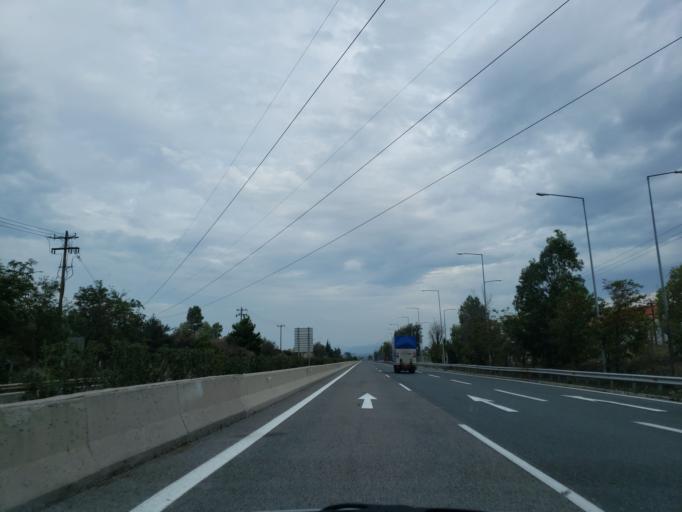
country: GR
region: Central Greece
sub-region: Nomos Voiotias
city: Schimatari
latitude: 38.3544
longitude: 23.5726
